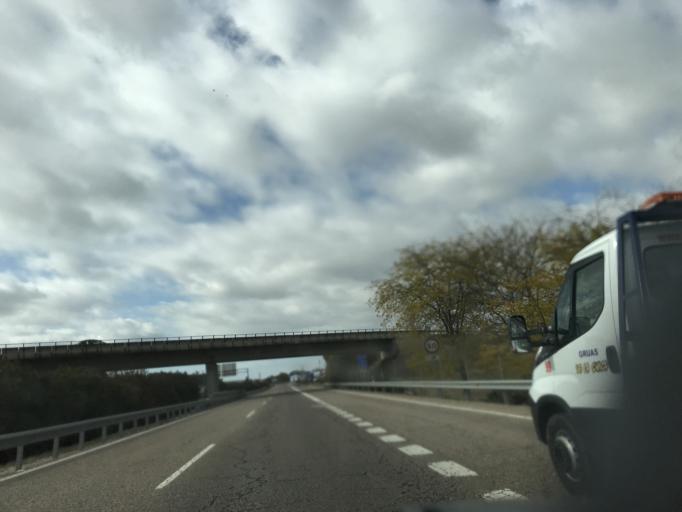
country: ES
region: Andalusia
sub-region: Provincia de Jaen
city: Andujar
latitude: 38.0304
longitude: -4.0528
